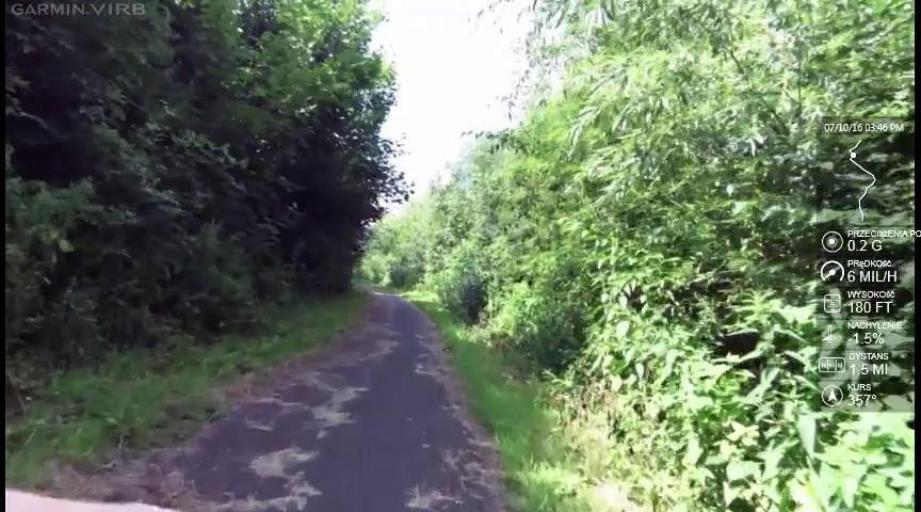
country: PL
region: West Pomeranian Voivodeship
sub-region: Powiat gryfinski
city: Banie
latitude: 53.1324
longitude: 14.6183
